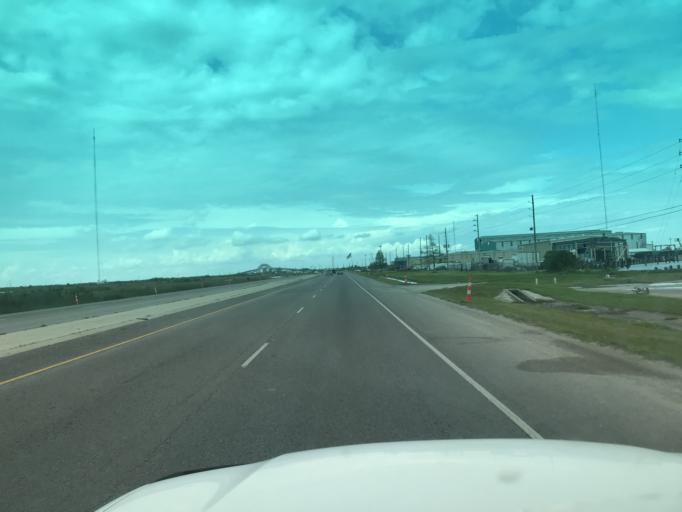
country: US
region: Louisiana
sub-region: Saint Bernard Parish
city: Chalmette
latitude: 29.9715
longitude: -89.9493
